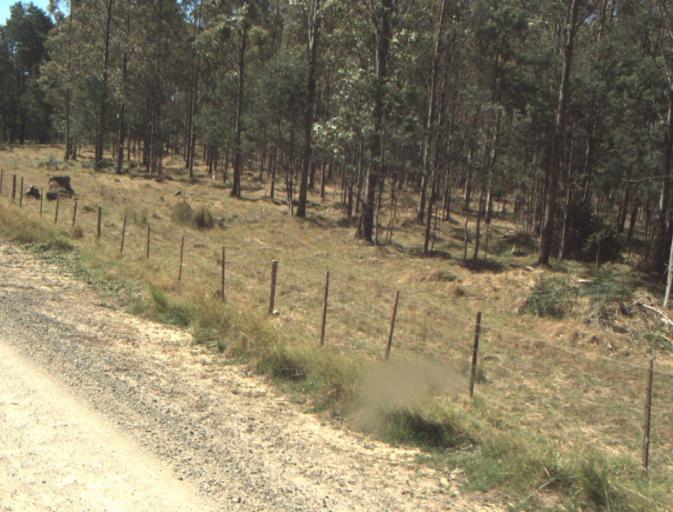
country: AU
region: Tasmania
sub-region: Dorset
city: Scottsdale
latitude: -41.3348
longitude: 147.4337
